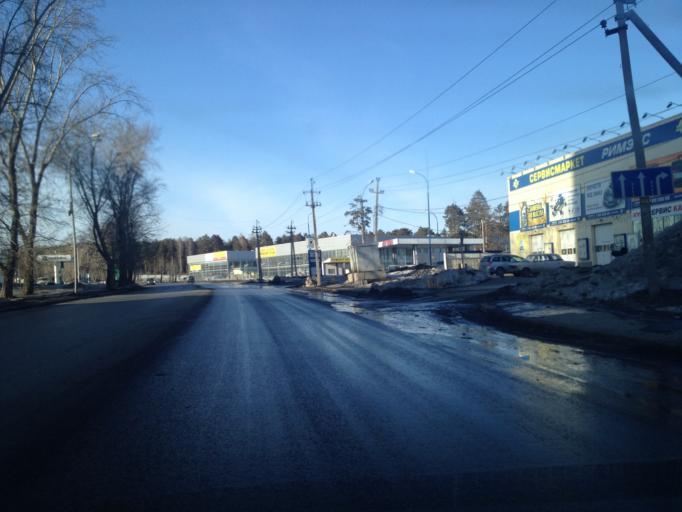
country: RU
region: Sverdlovsk
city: Yekaterinburg
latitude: 56.9103
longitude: 60.6197
